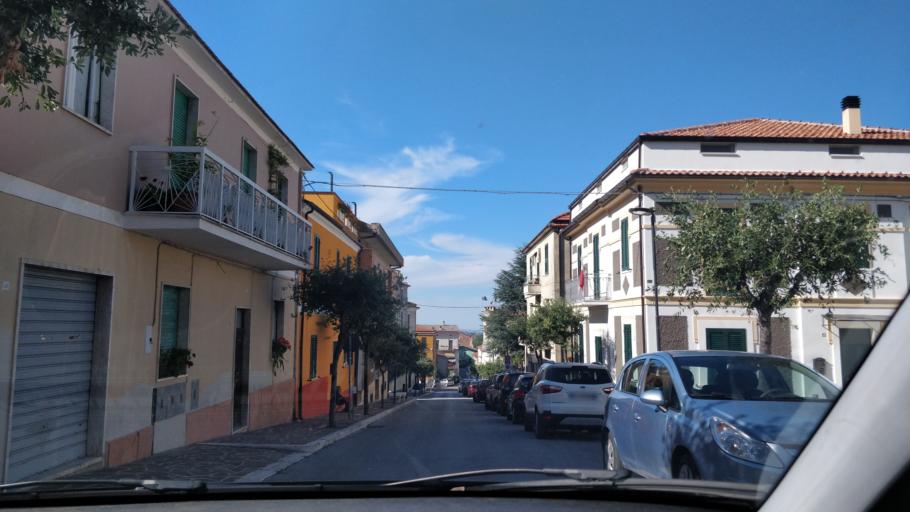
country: IT
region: Abruzzo
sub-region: Provincia di Pescara
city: Serramonacesca
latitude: 42.2479
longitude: 14.0930
